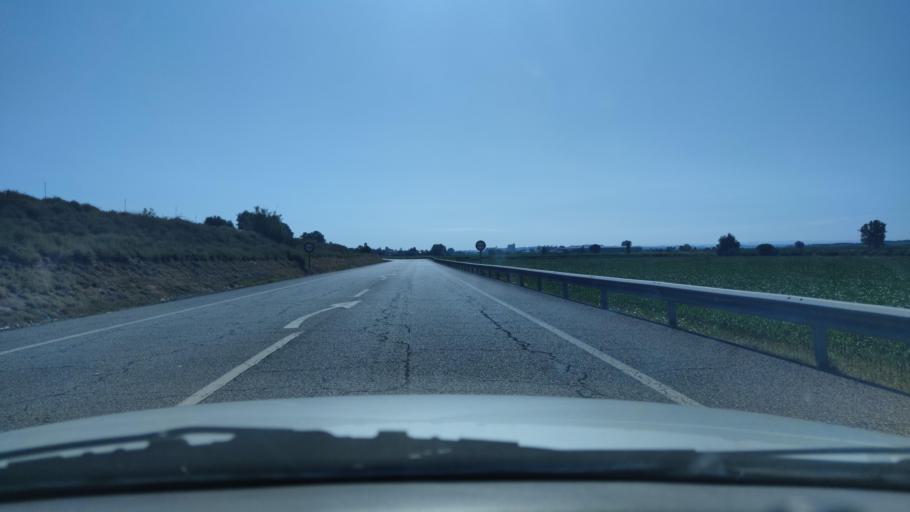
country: ES
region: Catalonia
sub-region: Provincia de Lleida
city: Sidamon
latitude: 41.6285
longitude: 0.7645
